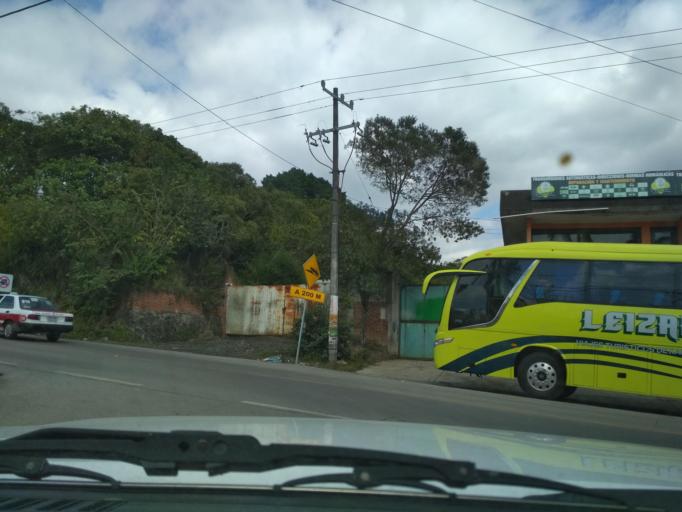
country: MX
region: Veracruz
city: Coatepec
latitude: 19.4524
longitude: -96.9445
